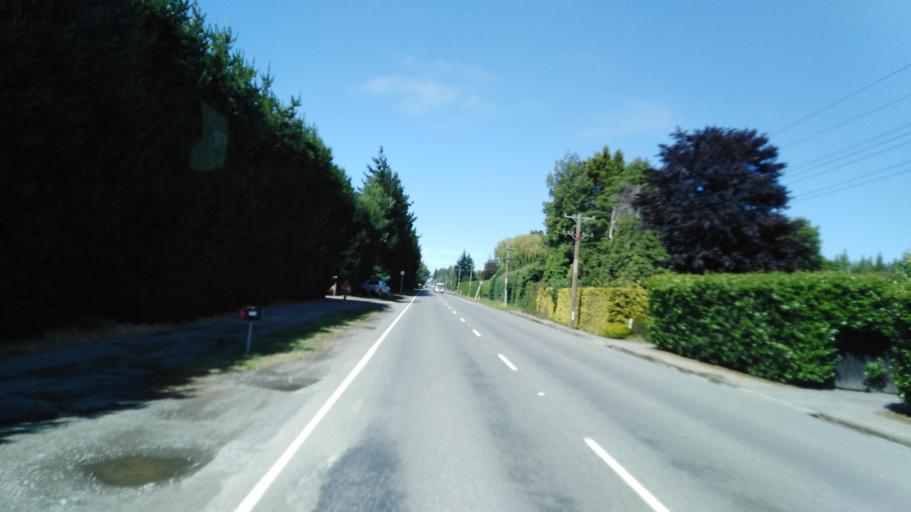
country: NZ
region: Canterbury
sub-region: Selwyn District
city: Prebbleton
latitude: -43.5146
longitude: 172.5078
